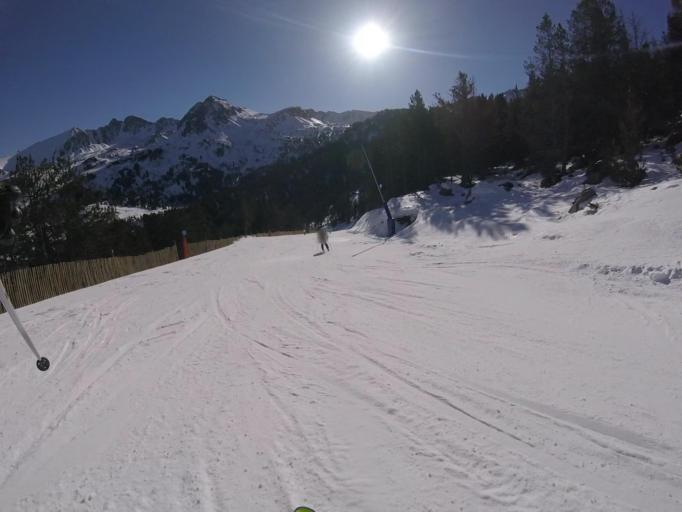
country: AD
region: Encamp
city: Pas de la Casa
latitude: 42.5296
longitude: 1.6913
